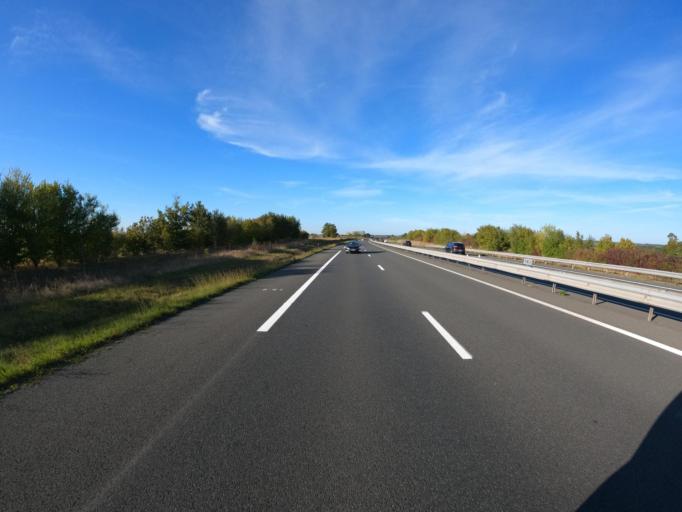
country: FR
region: Pays de la Loire
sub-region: Departement de Maine-et-Loire
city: Saint-Lambert-du-Lattay
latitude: 47.2802
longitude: -0.6164
